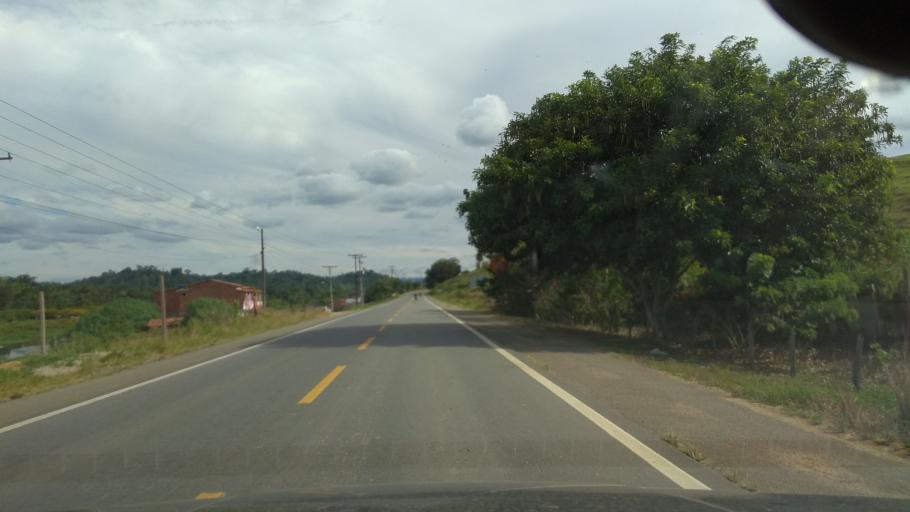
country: BR
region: Bahia
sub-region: Jitauna
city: Jitauna
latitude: -14.0134
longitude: -39.8811
